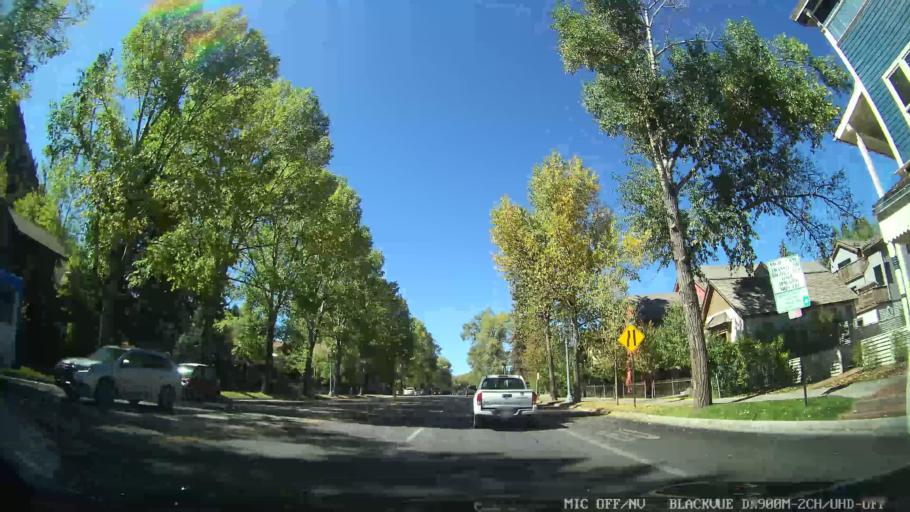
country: US
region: Colorado
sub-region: Pitkin County
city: Aspen
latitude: 39.1924
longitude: -106.8273
